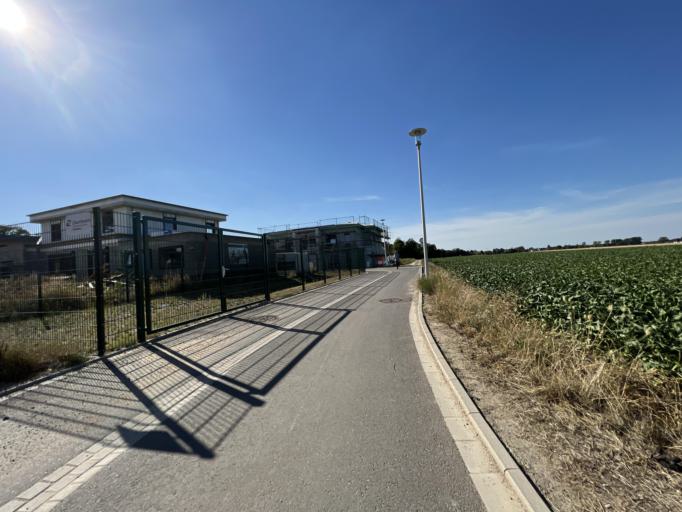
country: DE
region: North Rhine-Westphalia
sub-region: Regierungsbezirk Koln
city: Dueren
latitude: 50.7778
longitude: 6.4471
